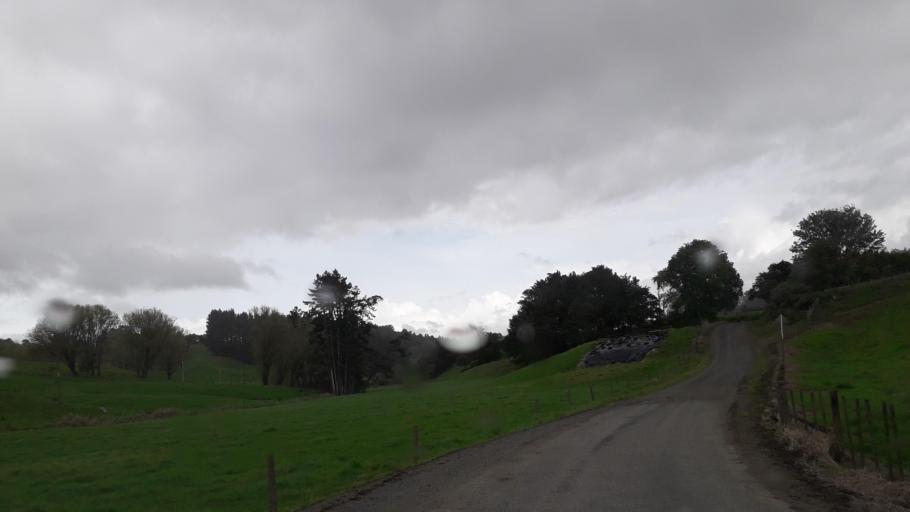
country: NZ
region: Northland
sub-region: Far North District
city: Waimate North
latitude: -35.2989
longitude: 173.5658
